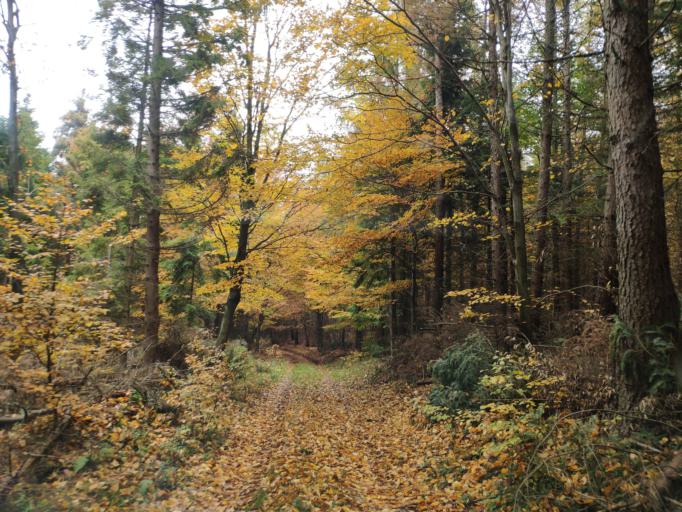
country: SK
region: Kosicky
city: Medzev
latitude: 48.7411
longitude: 20.9914
